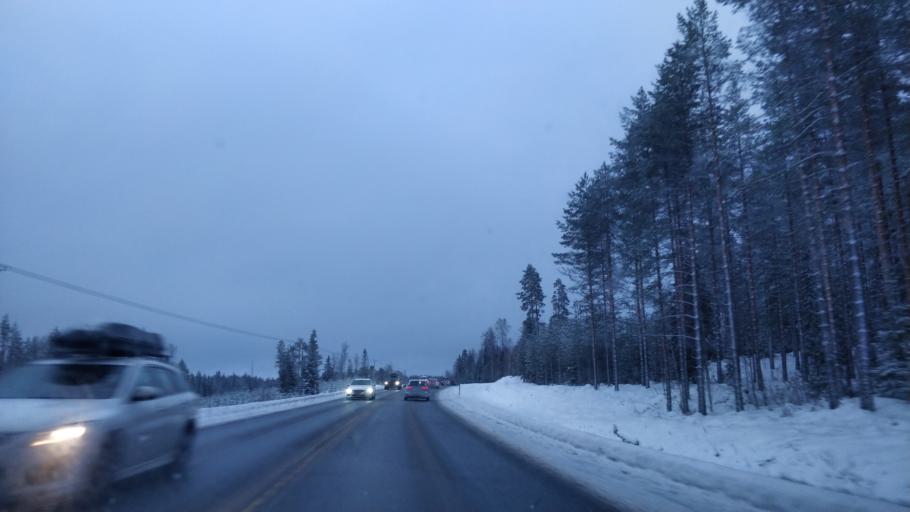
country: FI
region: Central Finland
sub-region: Saarijaervi-Viitasaari
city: Viitasaari
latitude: 63.1890
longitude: 25.7127
